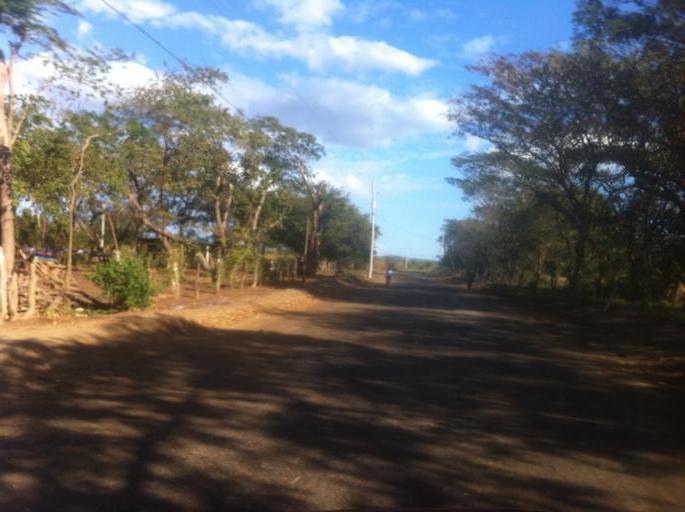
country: NI
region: Managua
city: Carlos Fonseca Amador
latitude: 11.8868
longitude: -86.5837
